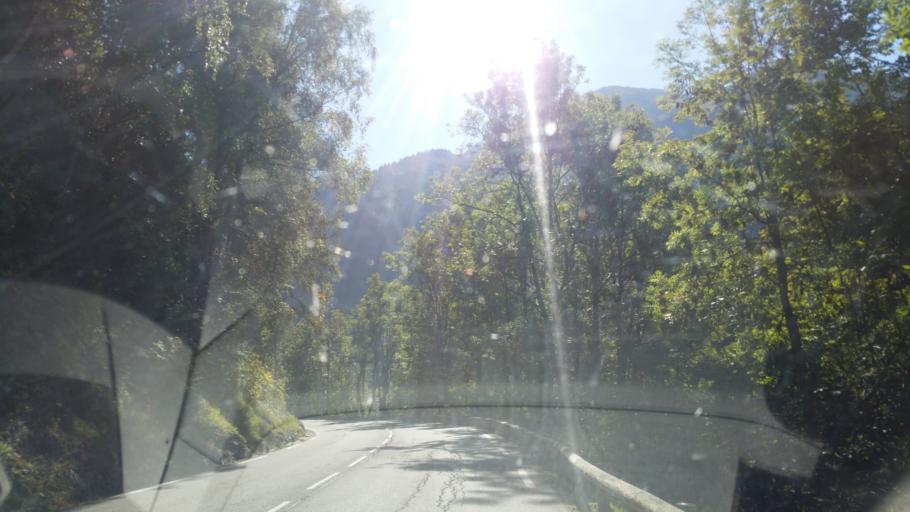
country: FR
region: Rhone-Alpes
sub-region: Departement de la Savoie
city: Seez
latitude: 45.5832
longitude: 6.8845
